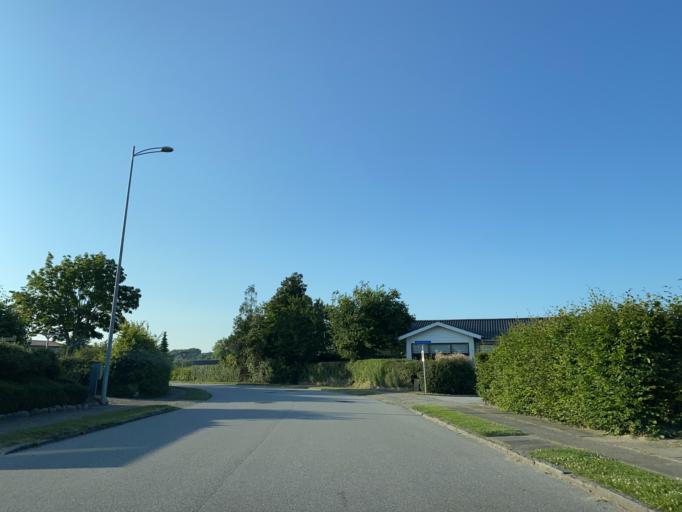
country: DK
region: South Denmark
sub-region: Aabenraa Kommune
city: Aabenraa
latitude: 55.0586
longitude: 9.4323
